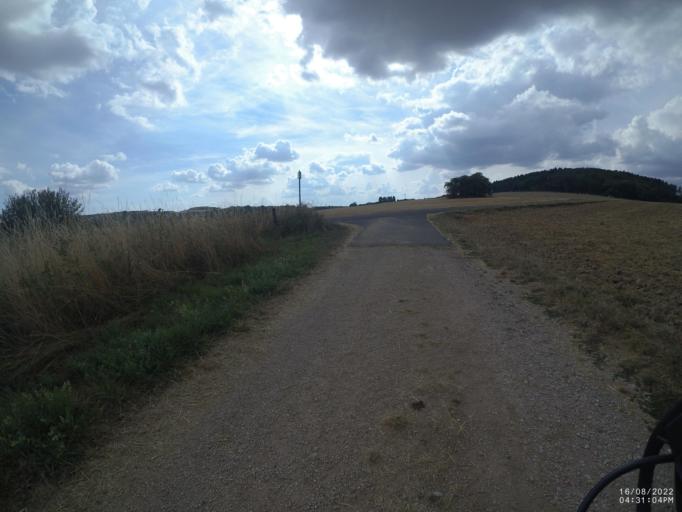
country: DE
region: Rheinland-Pfalz
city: Berndorf
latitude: 50.2958
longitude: 6.7008
